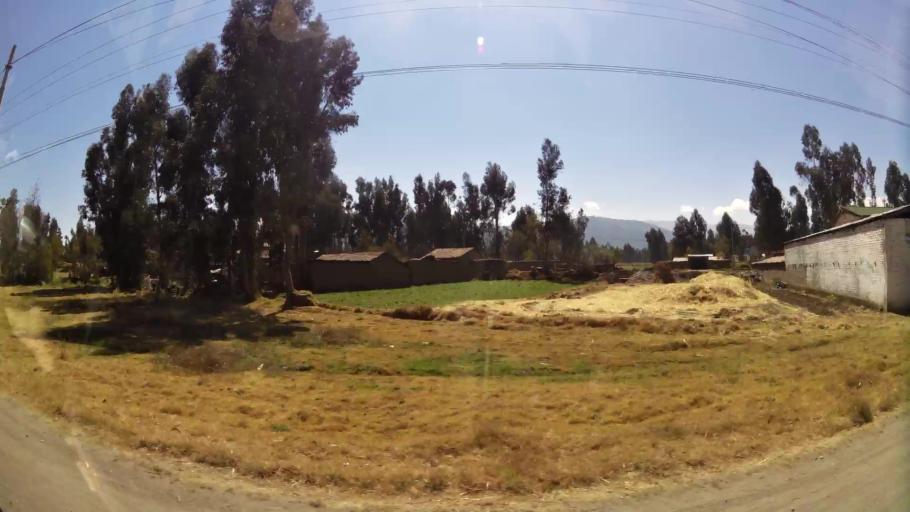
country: PE
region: Junin
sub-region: Provincia de Concepcion
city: Matahuasi
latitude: -11.8887
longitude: -75.3455
